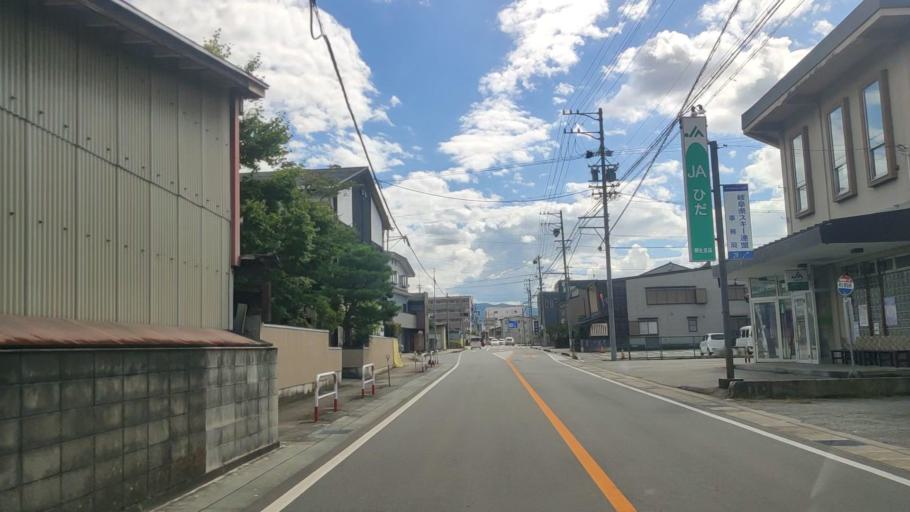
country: JP
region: Gifu
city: Takayama
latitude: 36.1544
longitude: 137.2540
